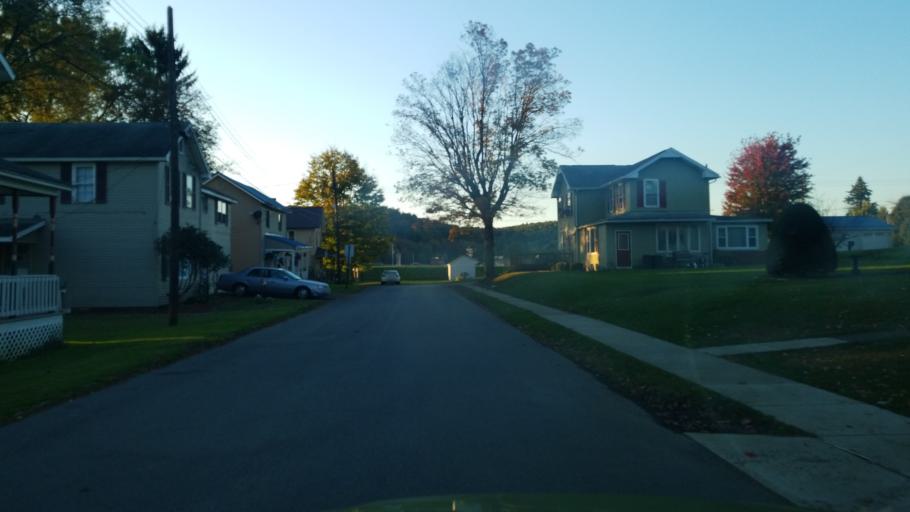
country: US
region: Pennsylvania
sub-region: Jefferson County
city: Reynoldsville
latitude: 41.0915
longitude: -78.8876
